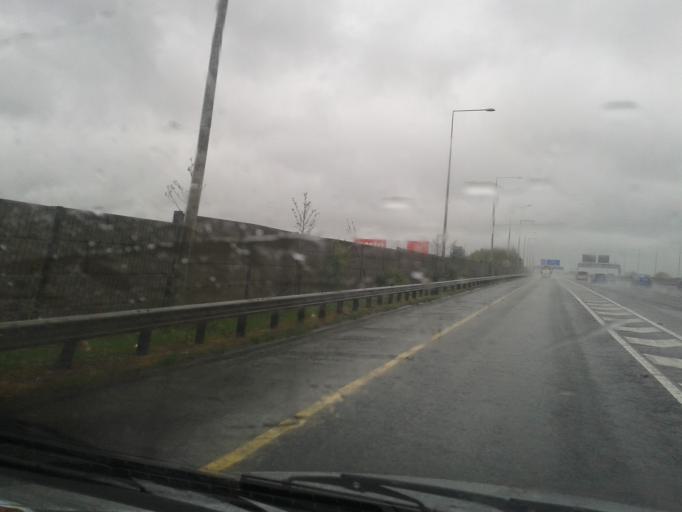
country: IE
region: Leinster
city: Beaumont
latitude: 53.4104
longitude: -6.2331
